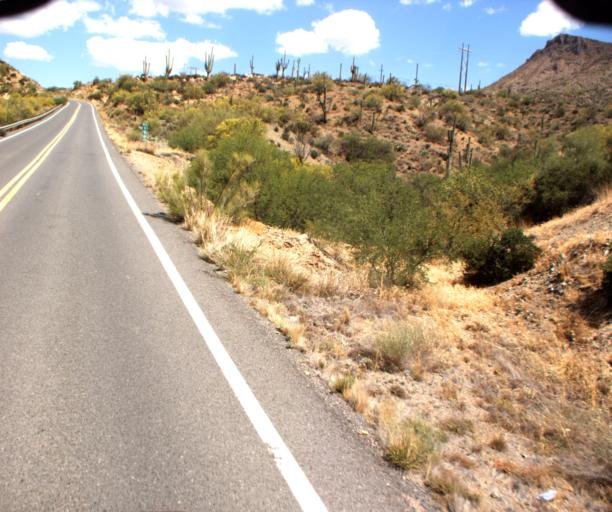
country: US
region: Arizona
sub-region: Pinal County
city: Superior
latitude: 33.1768
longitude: -111.0363
